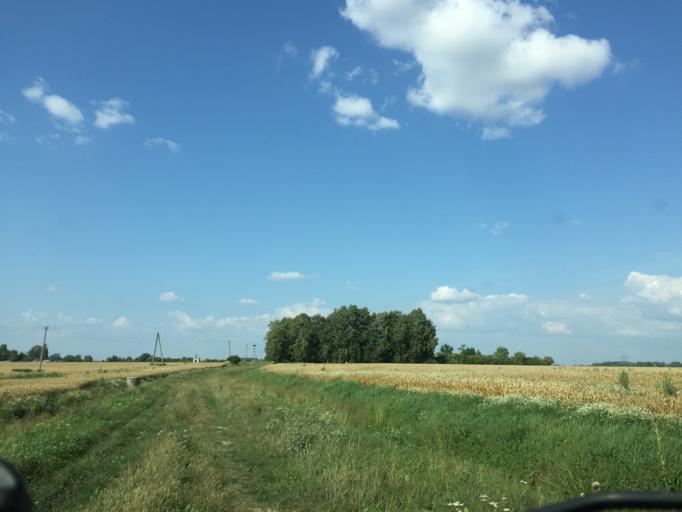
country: LV
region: Jelgava
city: Jelgava
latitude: 56.4718
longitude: 23.7053
